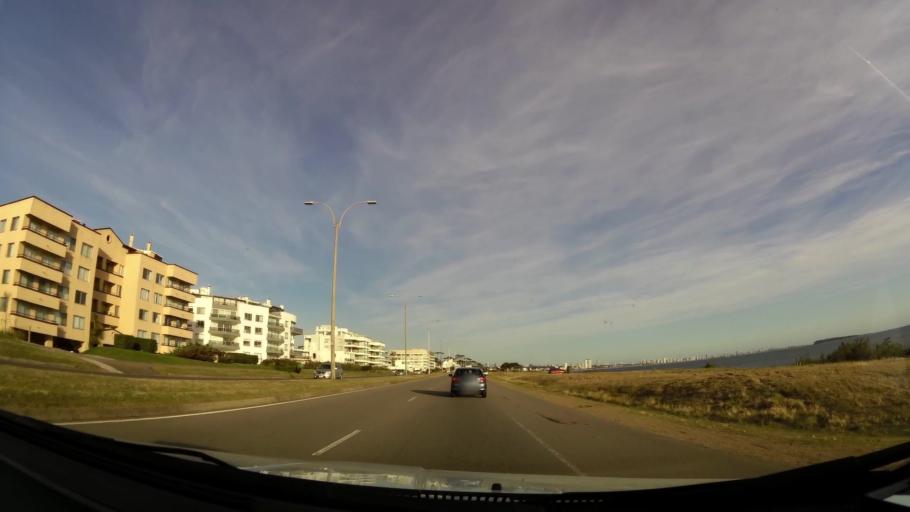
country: UY
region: Maldonado
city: Maldonado
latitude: -34.9098
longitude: -54.9992
